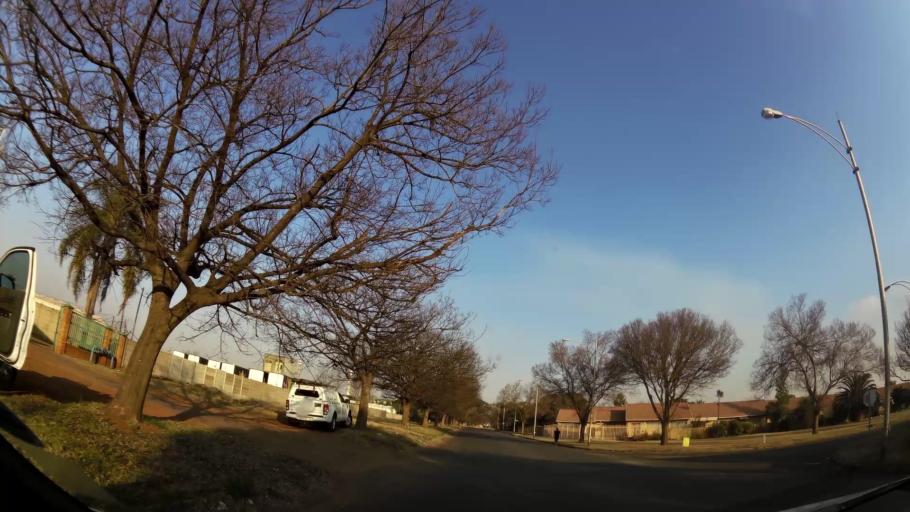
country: ZA
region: Gauteng
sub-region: Ekurhuleni Metropolitan Municipality
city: Springs
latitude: -26.2537
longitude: 28.4042
